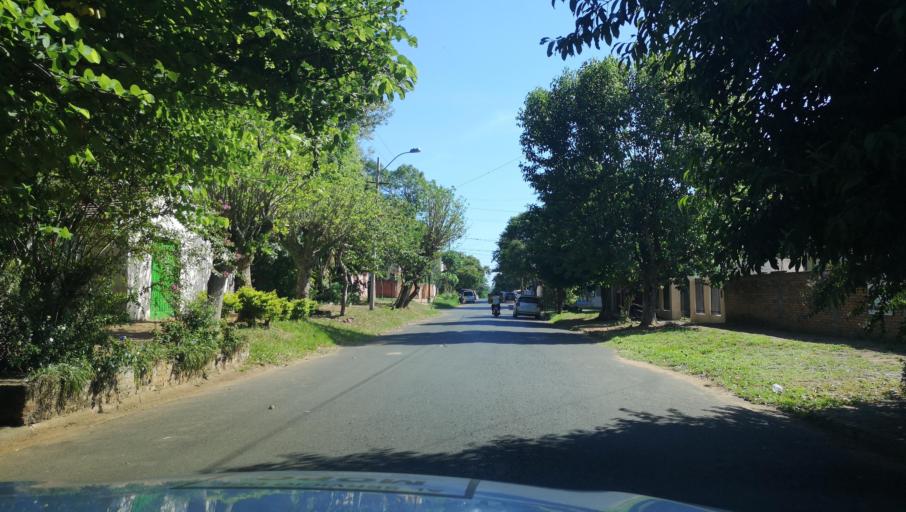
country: PY
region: Misiones
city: Santa Maria
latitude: -26.8908
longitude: -57.0222
